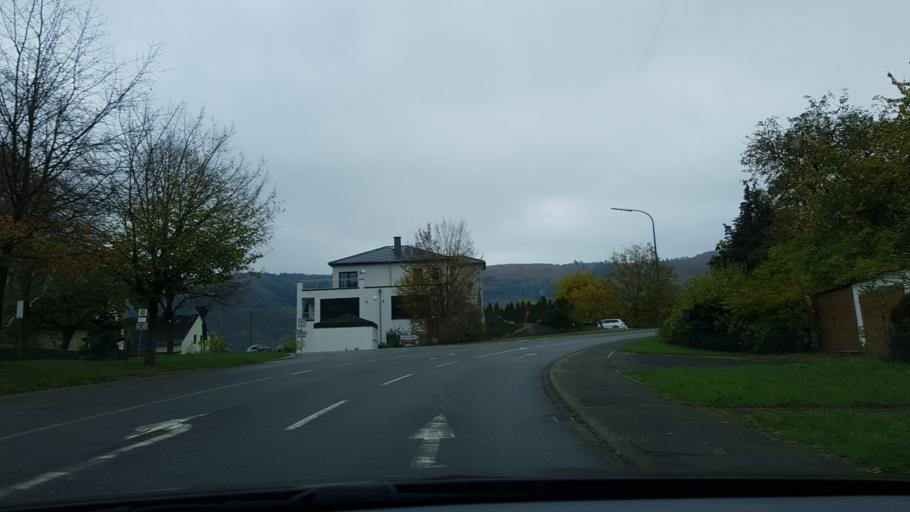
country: DE
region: Rheinland-Pfalz
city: Mehring
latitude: 49.7961
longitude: 6.8335
